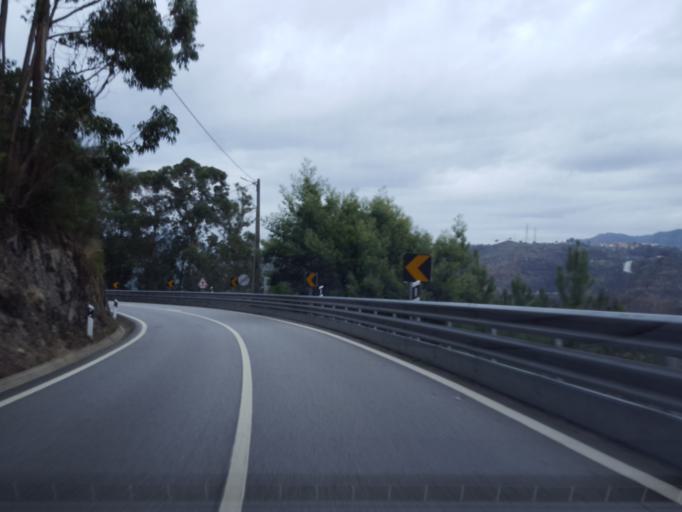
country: PT
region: Porto
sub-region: Marco de Canaveses
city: Marco de Canavezes
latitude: 41.1405
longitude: -8.1270
